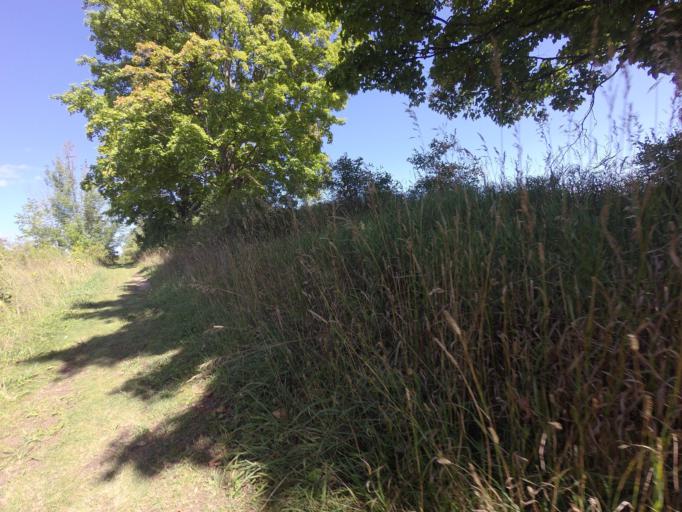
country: CA
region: Ontario
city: Orangeville
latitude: 43.8211
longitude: -80.0172
